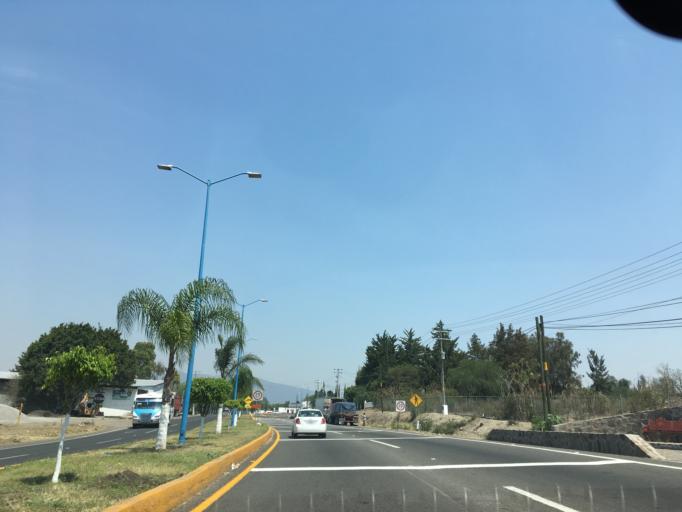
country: MX
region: Michoacan
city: Cuitzeo del Porvenir
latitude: 19.9623
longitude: -101.1380
